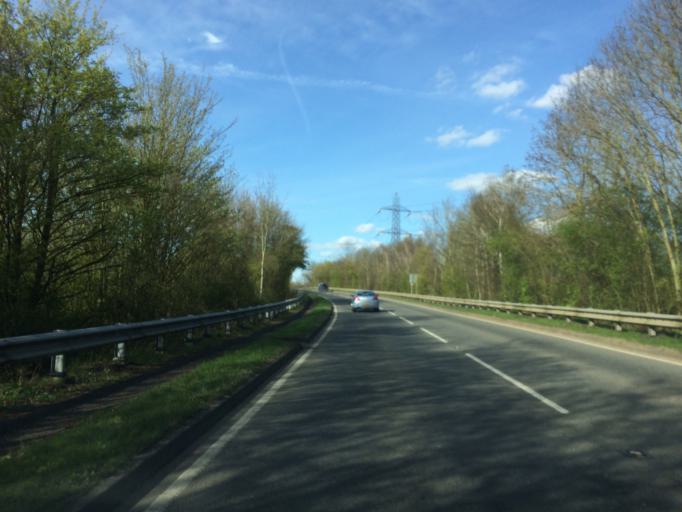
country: GB
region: England
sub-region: Surrey
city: Addlestone
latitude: 51.3916
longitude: -0.4789
